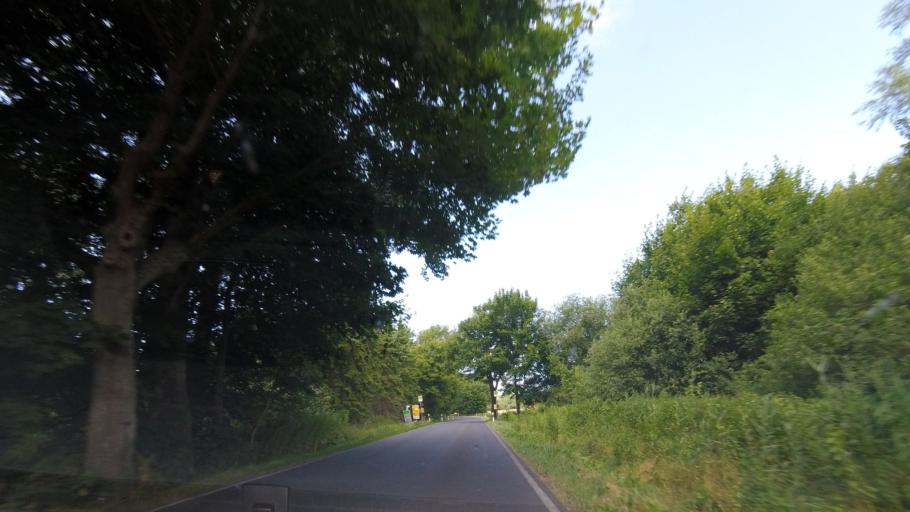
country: DE
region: Mecklenburg-Vorpommern
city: Wiek
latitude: 54.6439
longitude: 13.2949
